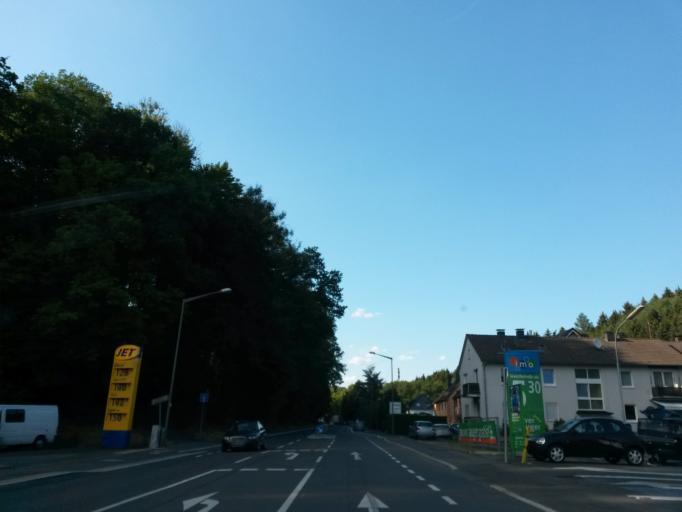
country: DE
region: North Rhine-Westphalia
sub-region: Regierungsbezirk Koln
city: Gummersbach
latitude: 51.0147
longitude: 7.5726
